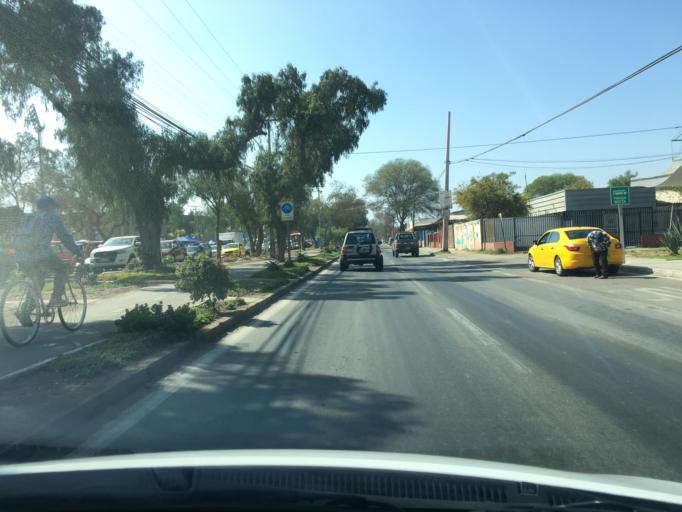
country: CL
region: Atacama
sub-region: Provincia de Copiapo
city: Copiapo
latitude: -27.3771
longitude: -70.3220
